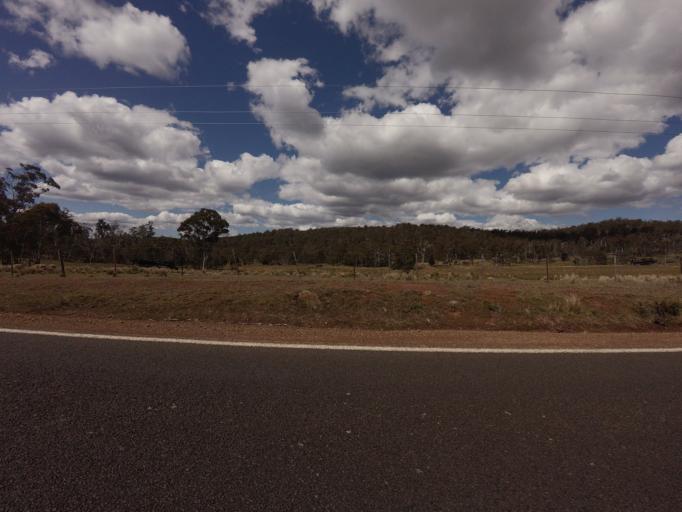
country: AU
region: Tasmania
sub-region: Northern Midlands
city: Evandale
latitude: -41.9533
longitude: 147.6112
